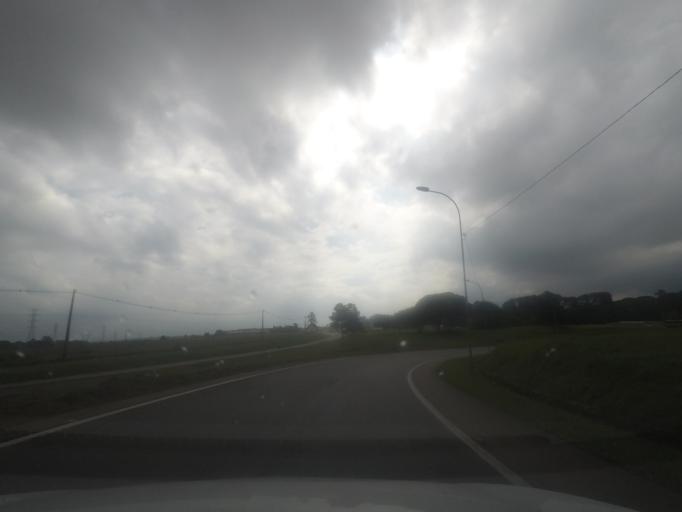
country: BR
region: Parana
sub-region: Sao Jose Dos Pinhais
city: Sao Jose dos Pinhais
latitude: -25.5456
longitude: -49.3049
